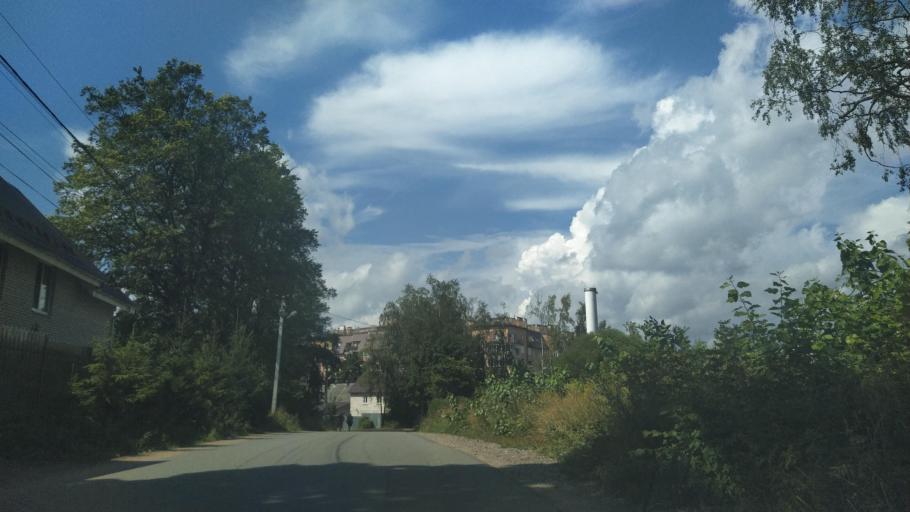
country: RU
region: Leningrad
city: Toksovo
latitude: 60.1657
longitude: 30.5410
